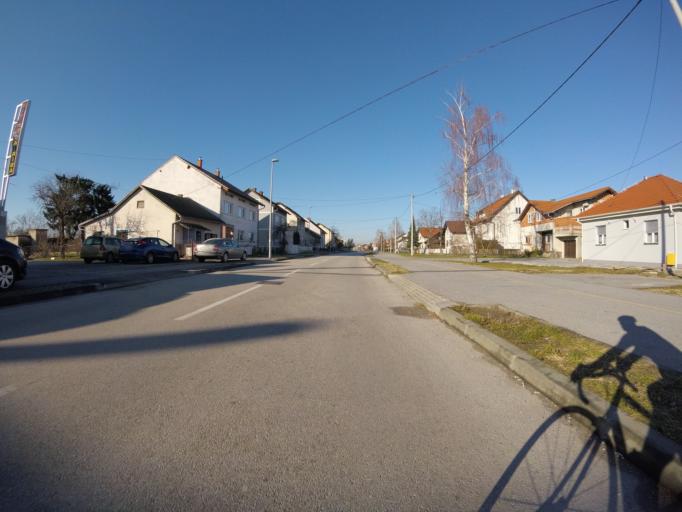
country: HR
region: Zagrebacka
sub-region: Grad Velika Gorica
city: Velika Gorica
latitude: 45.6983
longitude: 16.0724
